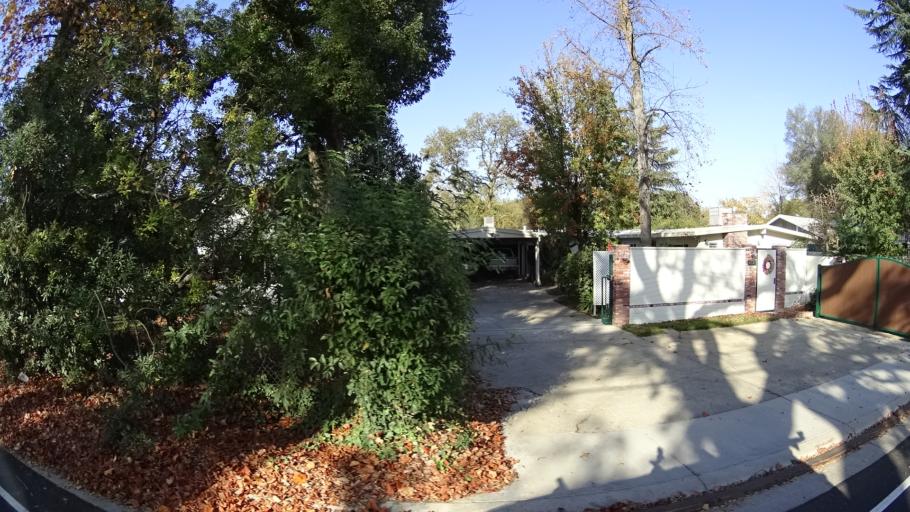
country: US
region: California
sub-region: Sacramento County
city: Citrus Heights
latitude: 38.6892
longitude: -121.2825
